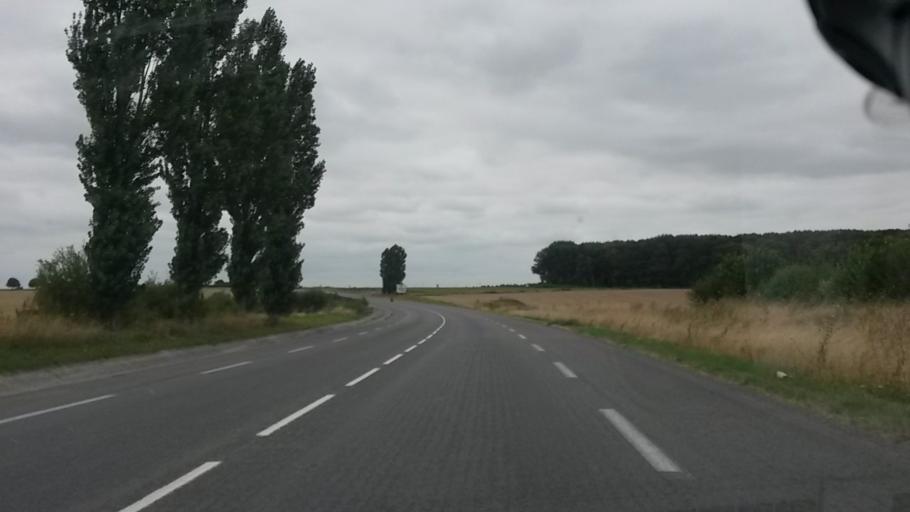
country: FR
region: Nord-Pas-de-Calais
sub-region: Departement du Pas-de-Calais
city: Bapaume
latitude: 50.1141
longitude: 2.8530
